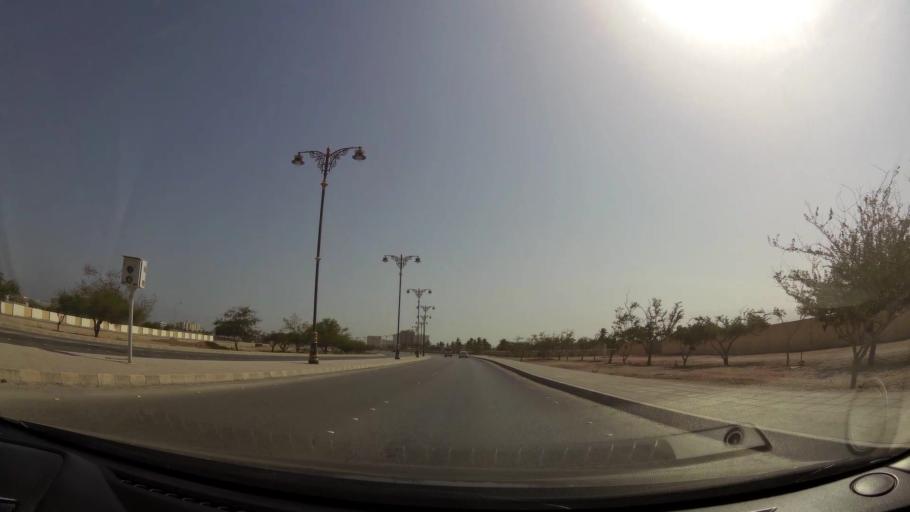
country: OM
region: Zufar
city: Salalah
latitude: 17.0107
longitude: 54.0457
